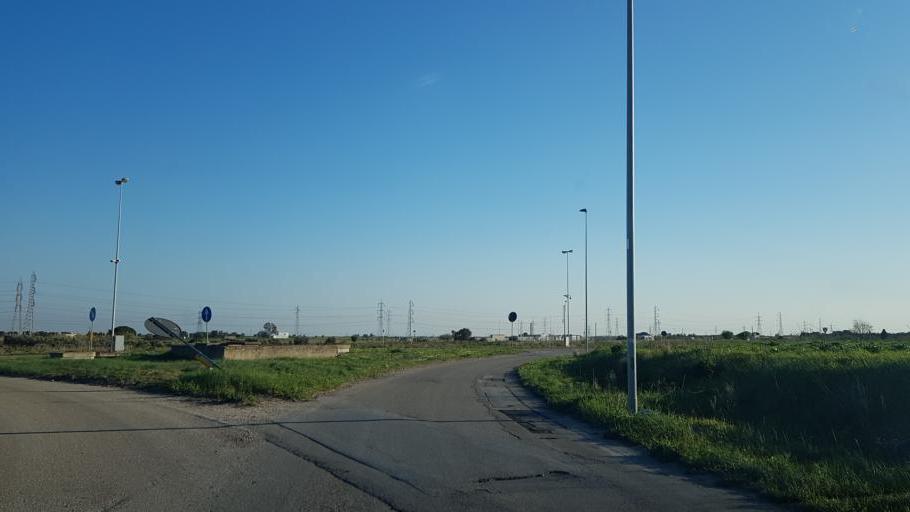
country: IT
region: Apulia
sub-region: Provincia di Brindisi
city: La Rosa
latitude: 40.6185
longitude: 17.9716
